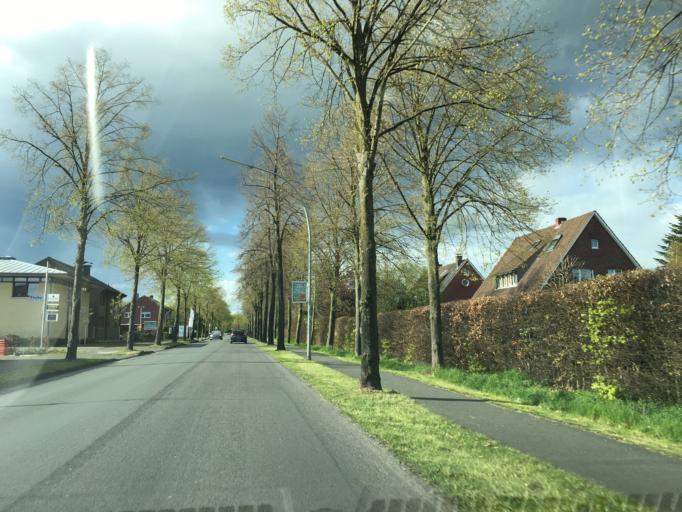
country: DE
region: North Rhine-Westphalia
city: Ludinghausen
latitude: 51.7689
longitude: 7.4594
